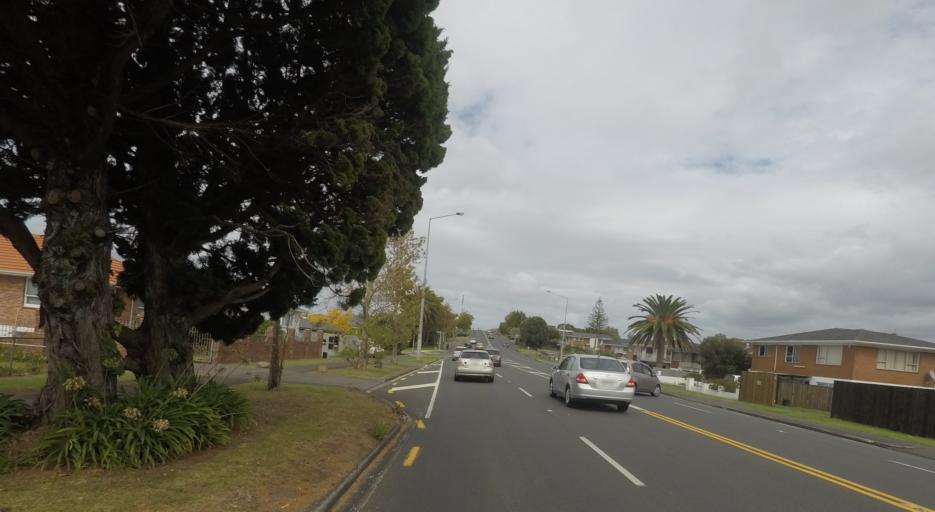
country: NZ
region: Auckland
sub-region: Auckland
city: Rosebank
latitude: -36.8890
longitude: 174.6447
